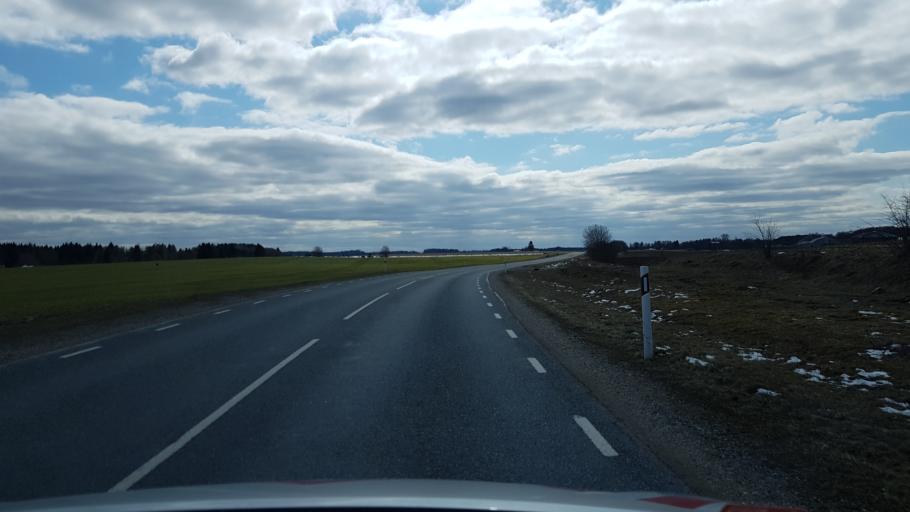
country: EE
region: Laeaene-Virumaa
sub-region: Tapa vald
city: Tapa
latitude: 59.3176
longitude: 26.0044
